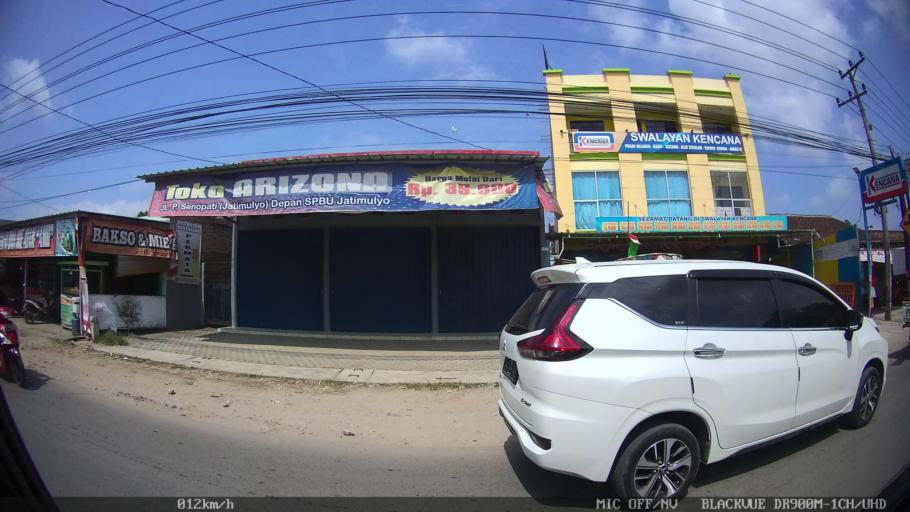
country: ID
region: Lampung
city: Kedaton
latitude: -5.3421
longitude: 105.2944
